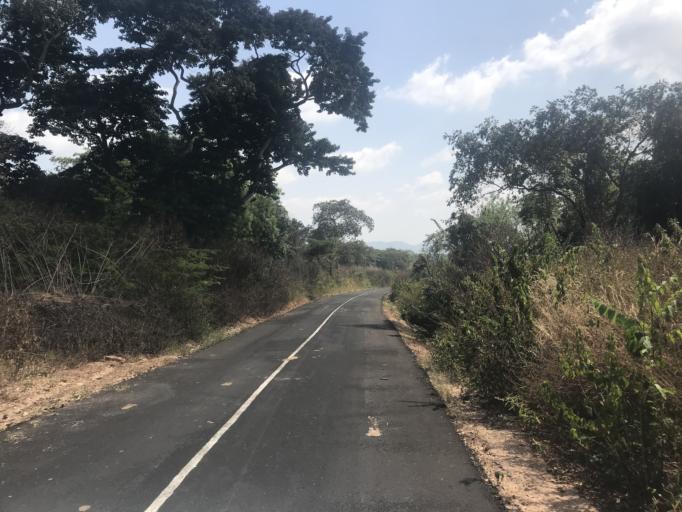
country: NG
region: Osun
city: Otan Ayegbaju
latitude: 7.8945
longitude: 4.8475
